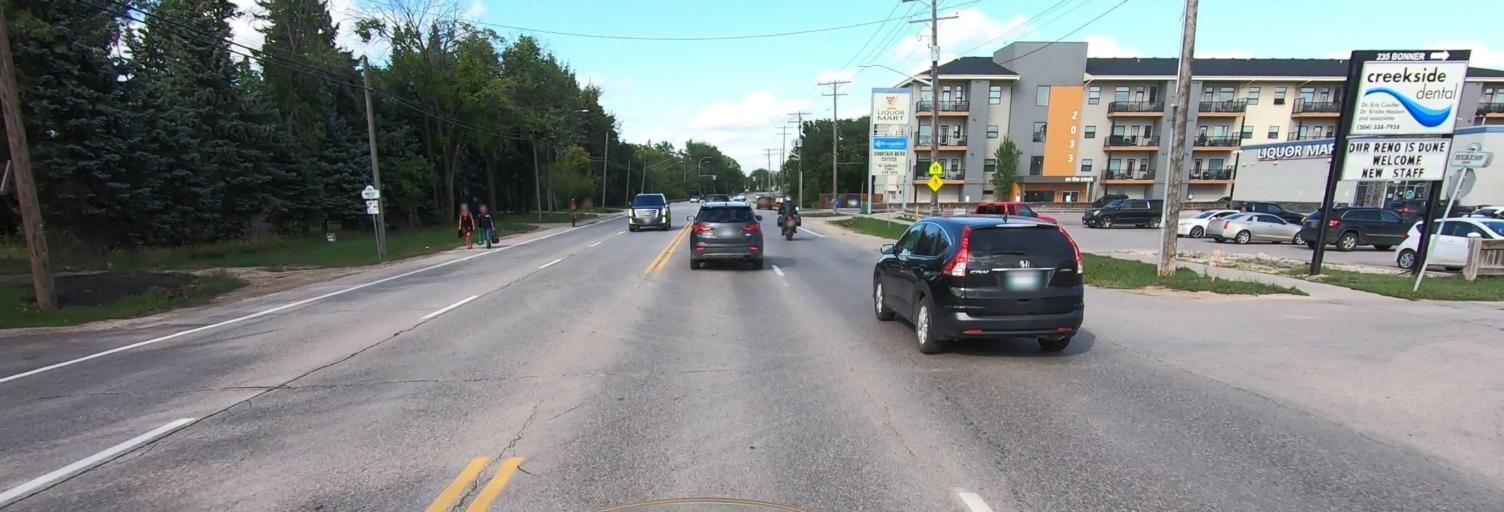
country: CA
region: Manitoba
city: Winnipeg
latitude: 49.9575
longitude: -97.0715
